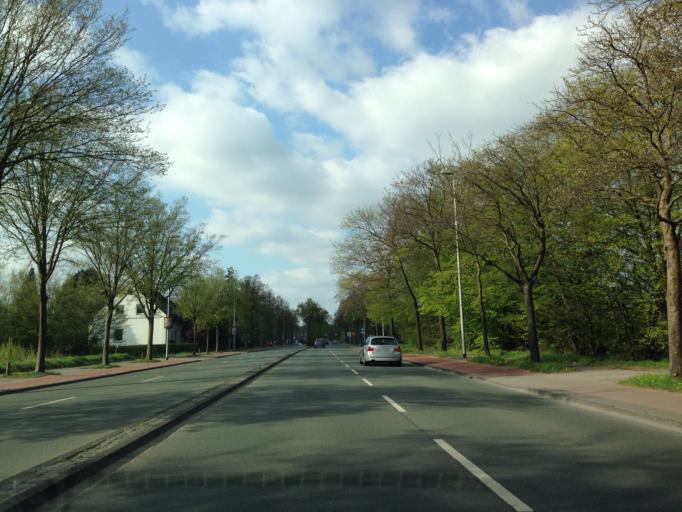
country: DE
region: North Rhine-Westphalia
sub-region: Regierungsbezirk Munster
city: Muenster
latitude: 51.9855
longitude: 7.6115
